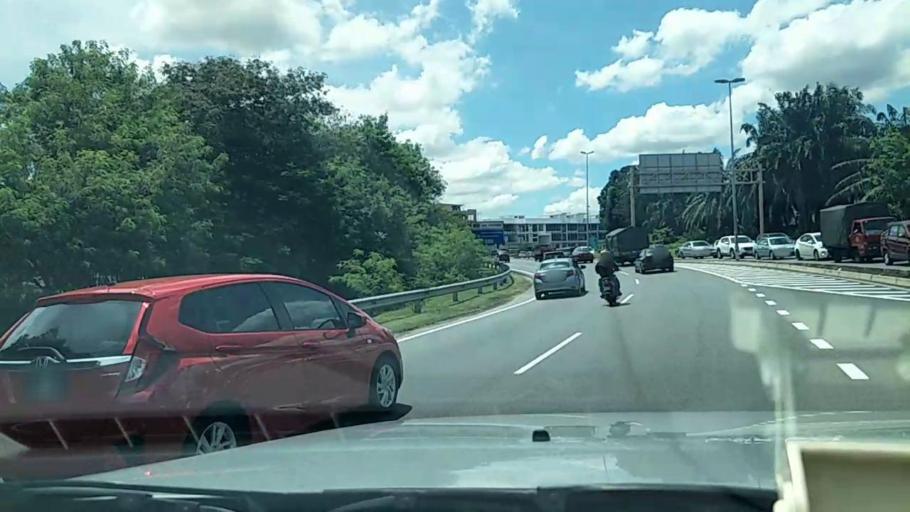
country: MY
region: Selangor
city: Subang Jaya
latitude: 2.9883
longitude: 101.6185
